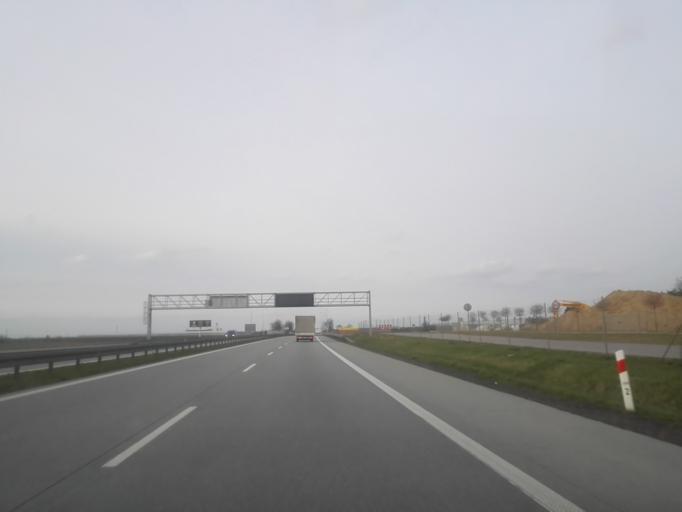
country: PL
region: Lodz Voivodeship
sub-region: Powiat rawski
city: Rawa Mazowiecka
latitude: 51.7980
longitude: 20.2947
